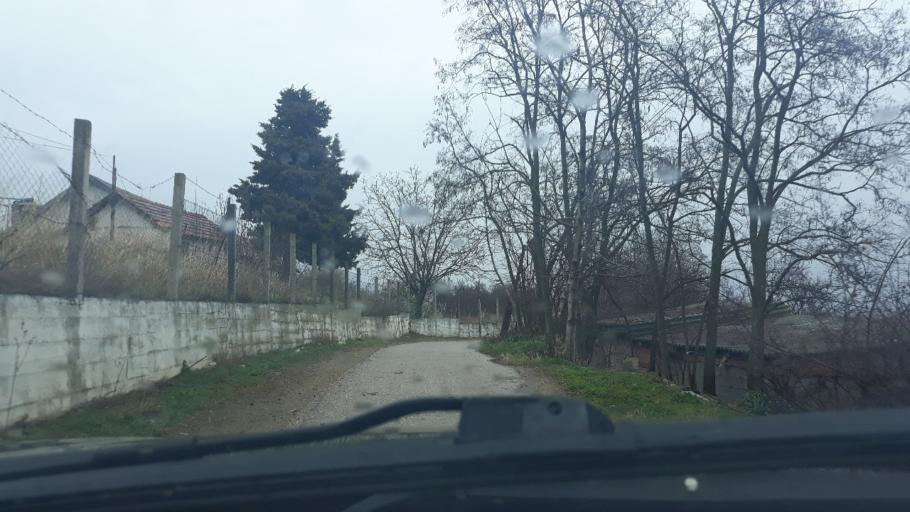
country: MK
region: Valandovo
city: Valandovo
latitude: 41.3178
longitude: 22.5470
